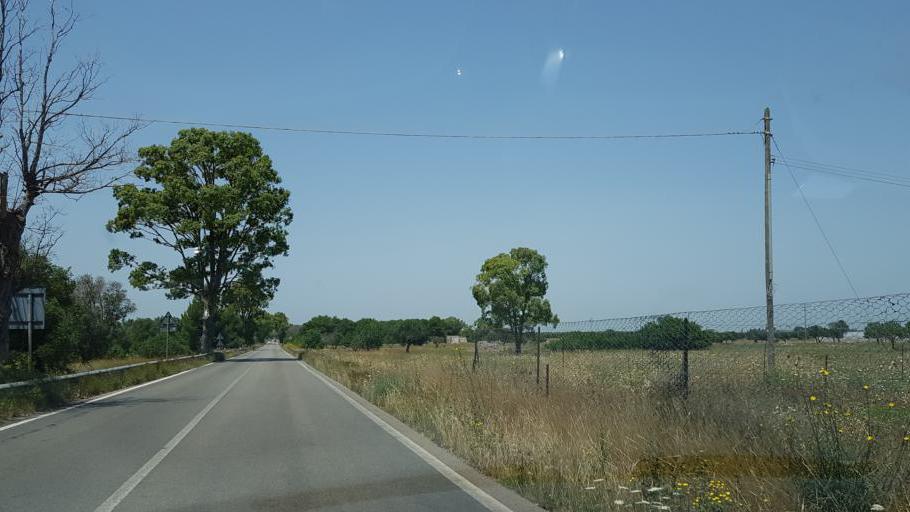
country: IT
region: Apulia
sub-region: Provincia di Lecce
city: Porto Cesareo
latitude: 40.2539
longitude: 17.9304
